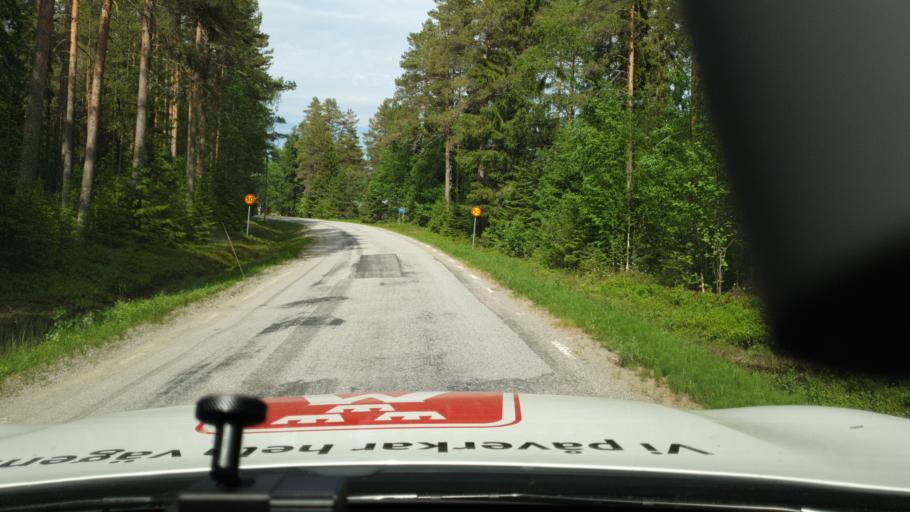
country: SE
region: Vaesterbotten
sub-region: Umea Kommun
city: Hoernefors
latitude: 63.5368
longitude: 19.7166
